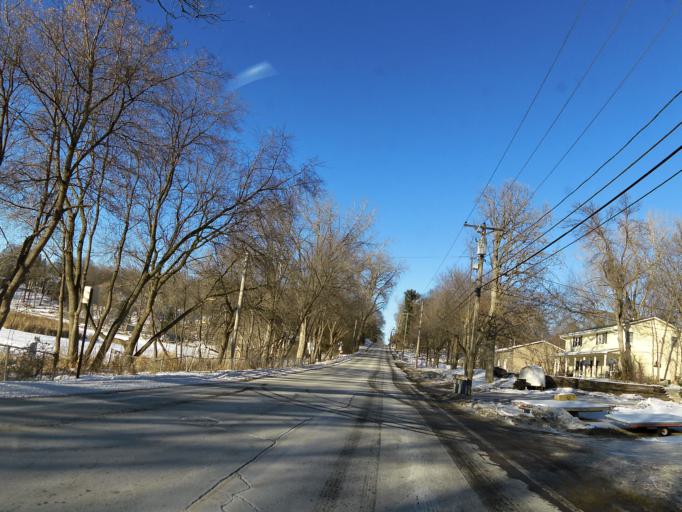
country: US
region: Minnesota
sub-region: Hennepin County
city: Mound
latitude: 44.9218
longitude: -93.6818
